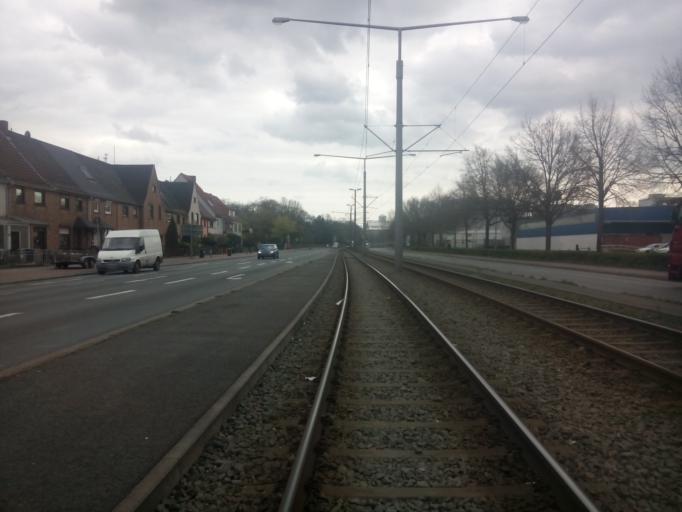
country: DE
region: Bremen
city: Bremen
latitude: 53.1081
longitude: 8.7645
